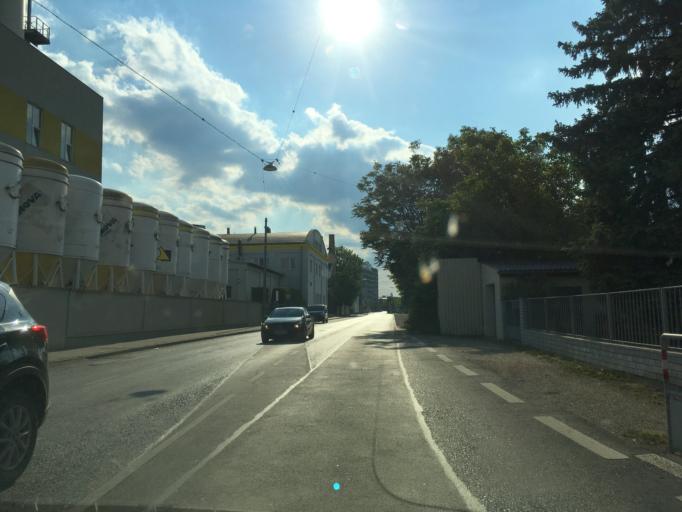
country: AT
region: Lower Austria
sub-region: Politischer Bezirk Modling
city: Vosendorf
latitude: 48.1413
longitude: 16.3235
